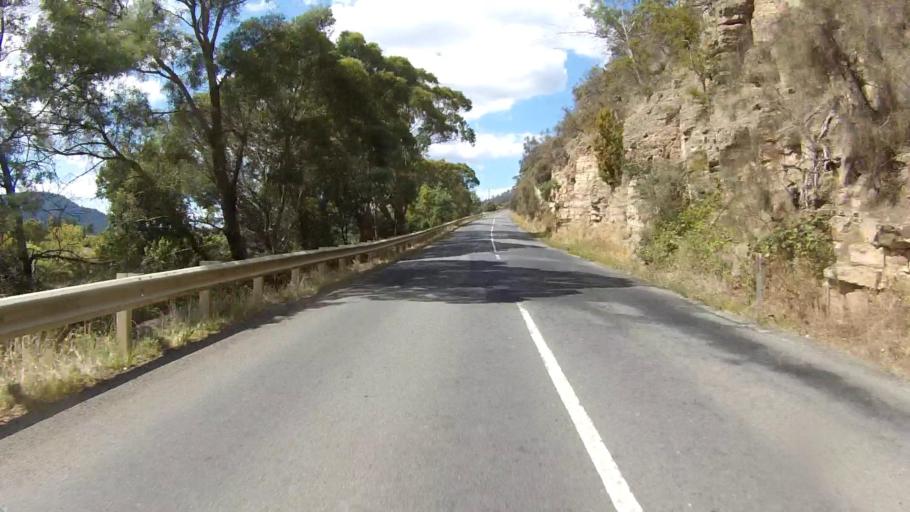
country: AU
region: Tasmania
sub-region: Derwent Valley
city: New Norfolk
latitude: -42.7790
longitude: 147.0327
